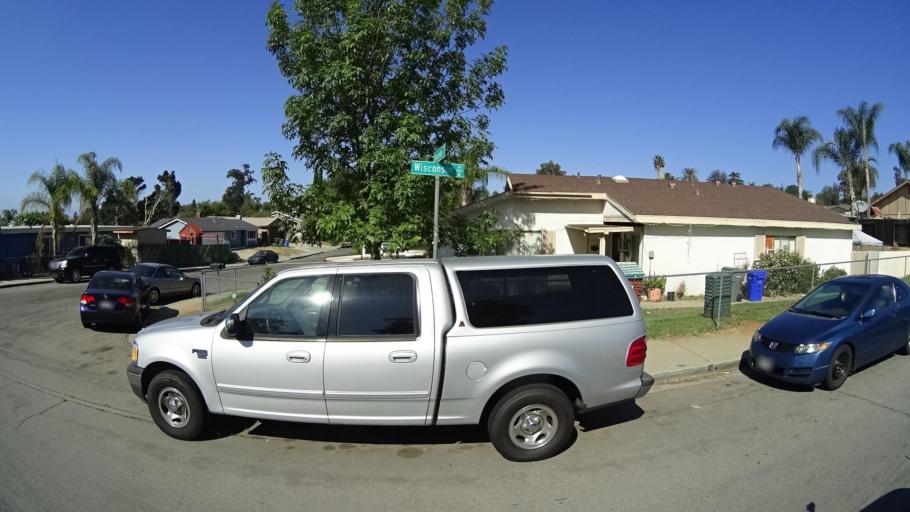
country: US
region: California
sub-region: San Diego County
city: Fallbrook
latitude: 33.3760
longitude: -117.2553
